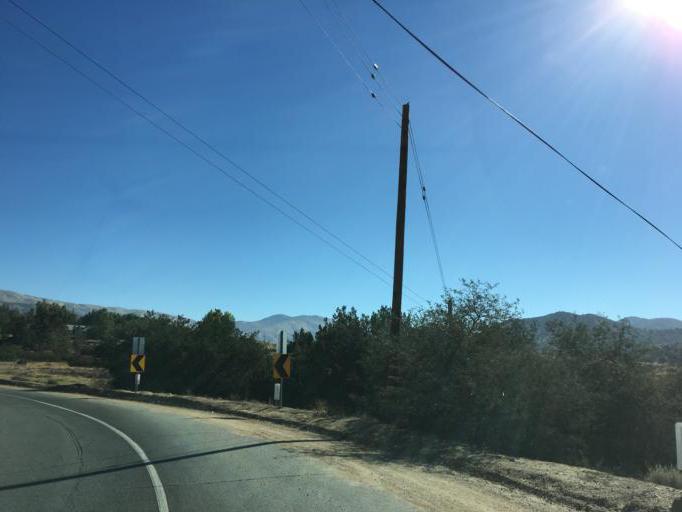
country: US
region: California
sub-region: Los Angeles County
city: Agua Dulce
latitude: 34.5001
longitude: -118.3248
